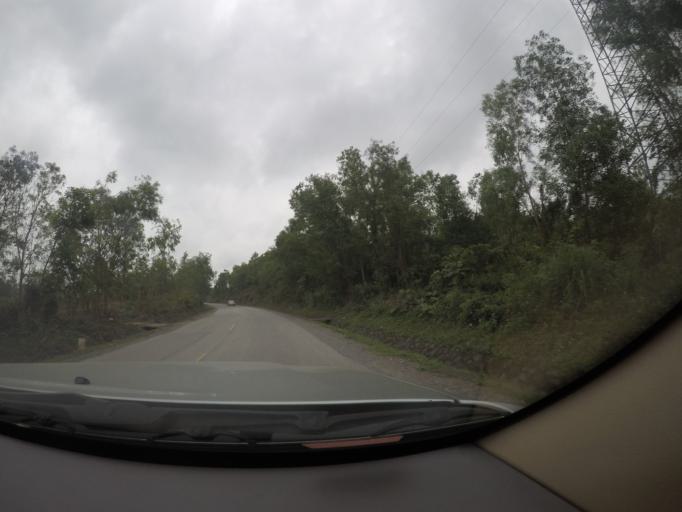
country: VN
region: Quang Binh
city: Quan Hau
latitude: 17.3210
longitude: 106.6240
